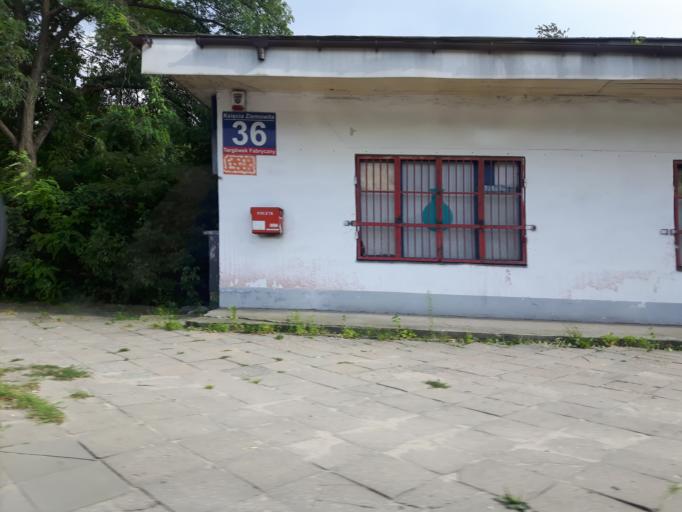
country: PL
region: Masovian Voivodeship
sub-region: Warszawa
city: Praga Poludnie
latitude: 52.2656
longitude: 21.0681
